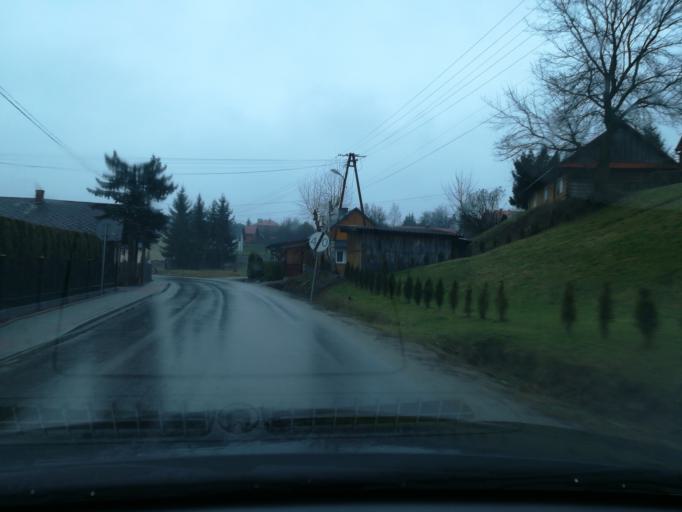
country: PL
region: Subcarpathian Voivodeship
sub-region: Powiat lancucki
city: Kosina
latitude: 50.0783
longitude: 22.3322
